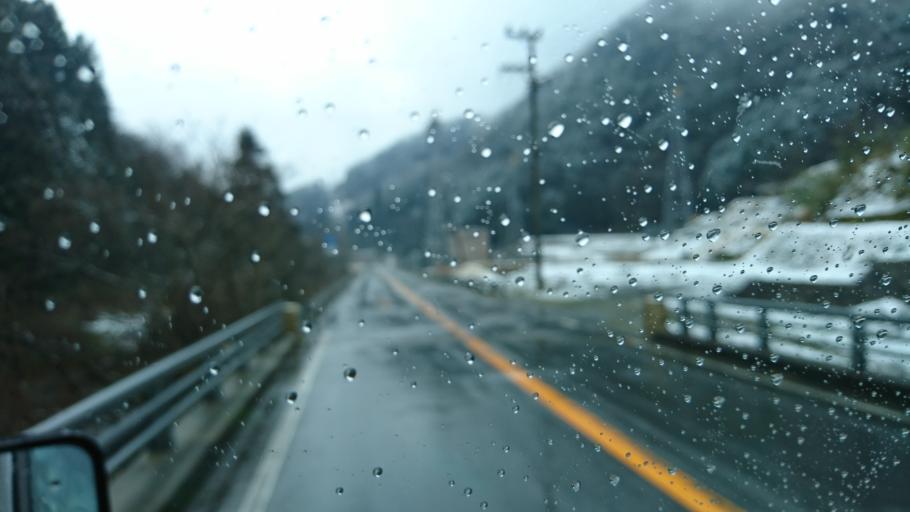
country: JP
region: Tottori
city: Tottori
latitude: 35.5408
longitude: 134.5076
